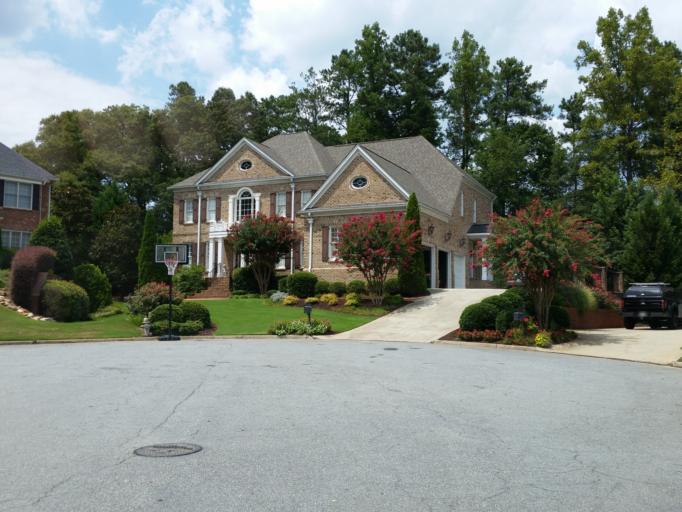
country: US
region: Georgia
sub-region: Fulton County
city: Sandy Springs
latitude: 33.9585
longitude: -84.4331
